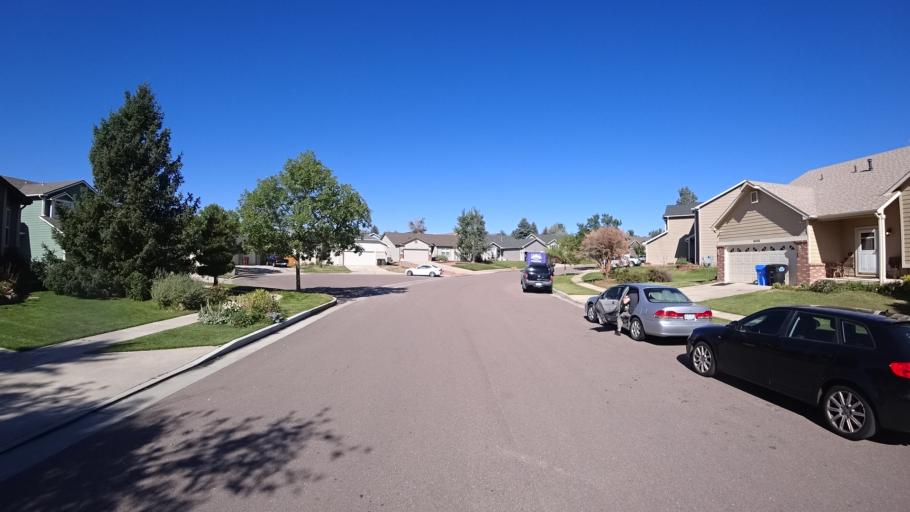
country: US
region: Colorado
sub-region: El Paso County
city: Black Forest
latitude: 38.9511
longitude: -104.7292
